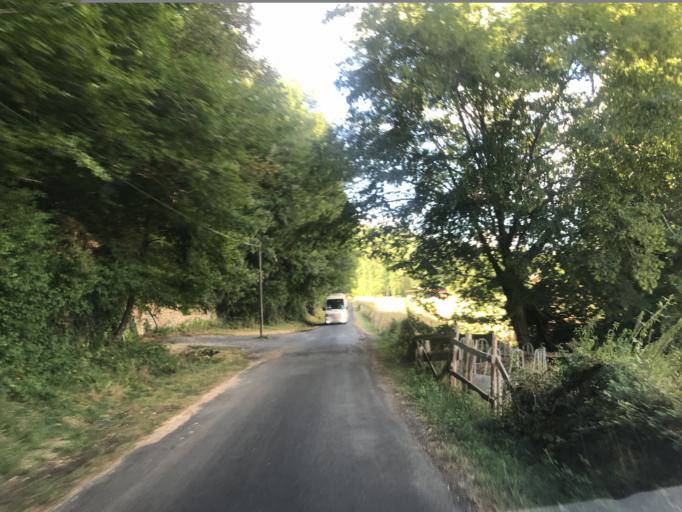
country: FR
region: Aquitaine
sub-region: Departement de la Dordogne
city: Rouffignac-Saint-Cernin-de-Reilhac
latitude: 44.9755
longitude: 1.0342
